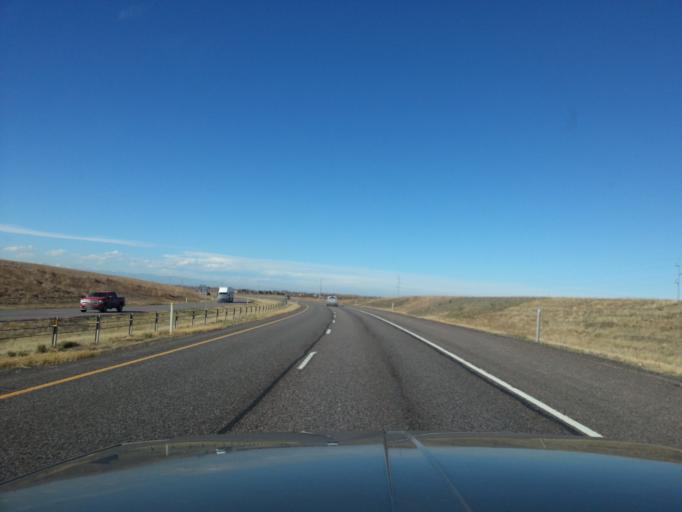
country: US
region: Colorado
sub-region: Adams County
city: Brighton
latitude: 39.9001
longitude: -104.7624
